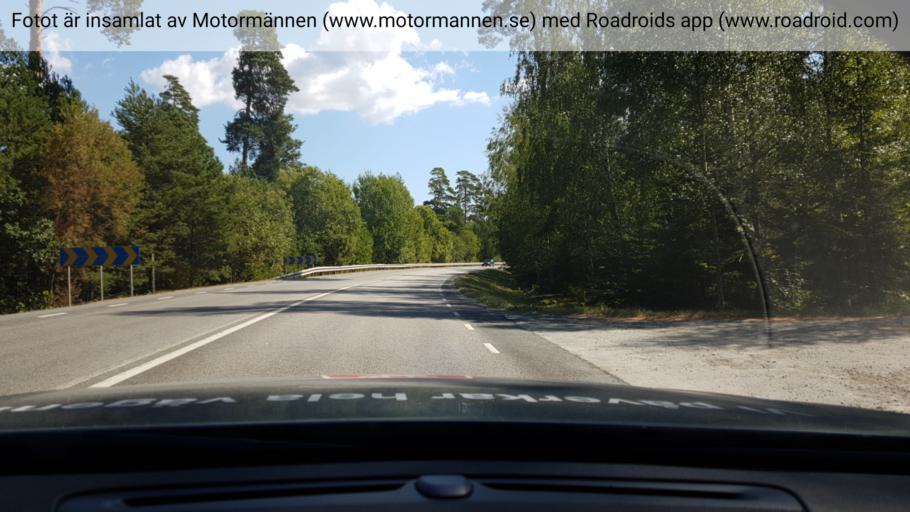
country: SE
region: Stockholm
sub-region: Ekero Kommun
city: Ekeroe
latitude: 59.3030
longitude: 17.8044
